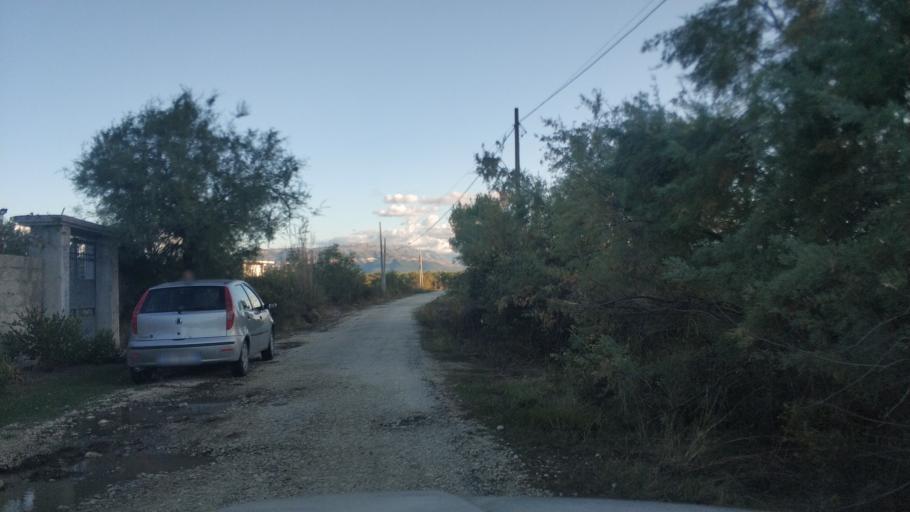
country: AL
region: Vlore
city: Vlore
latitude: 40.5092
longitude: 19.4225
